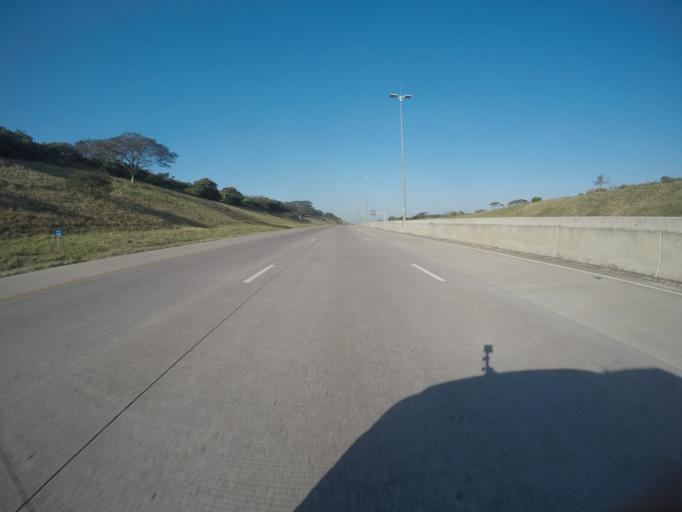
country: ZA
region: KwaZulu-Natal
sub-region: iLembe District Municipality
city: Ballitoville
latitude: -29.6073
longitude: 31.1365
